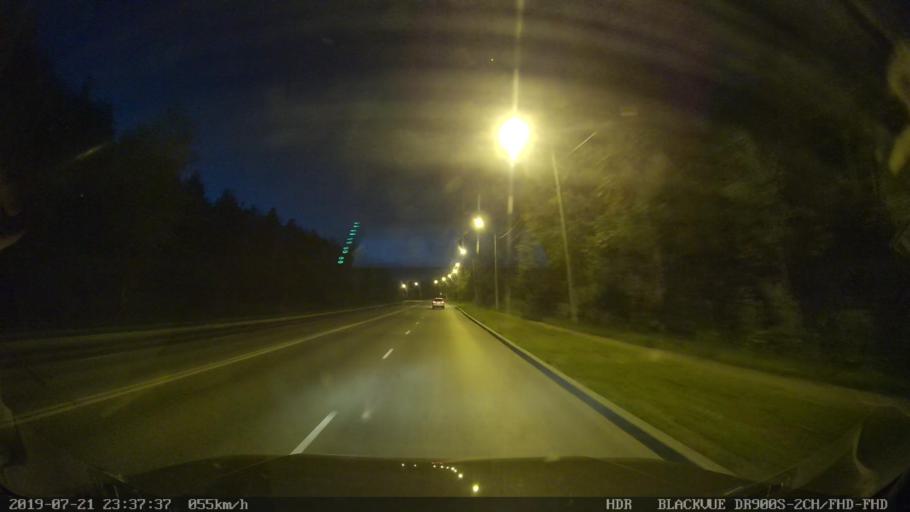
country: RU
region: Perm
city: Kondratovo
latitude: 57.9486
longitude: 56.1764
